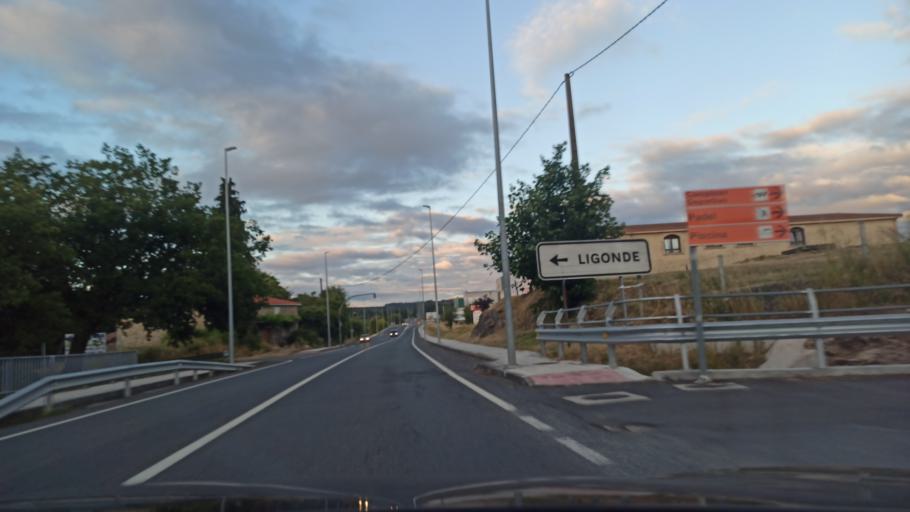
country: ES
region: Galicia
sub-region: Provincia de Lugo
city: Monterroso
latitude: 42.7955
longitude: -7.8223
